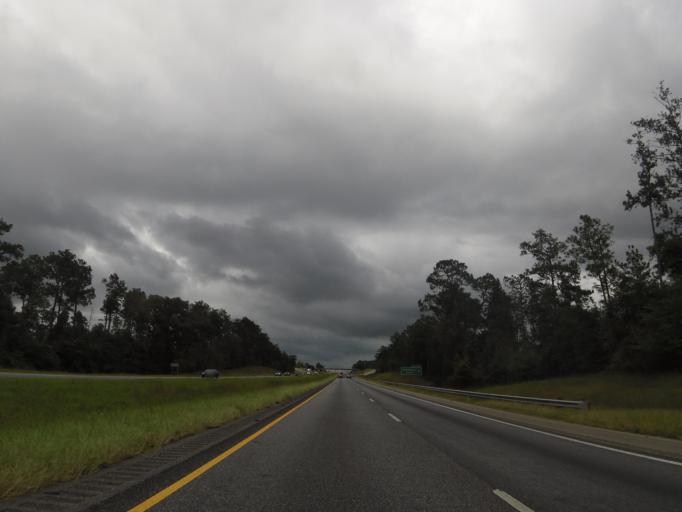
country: US
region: Alabama
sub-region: Conecuh County
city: Evergreen
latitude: 31.3254
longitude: -87.1331
